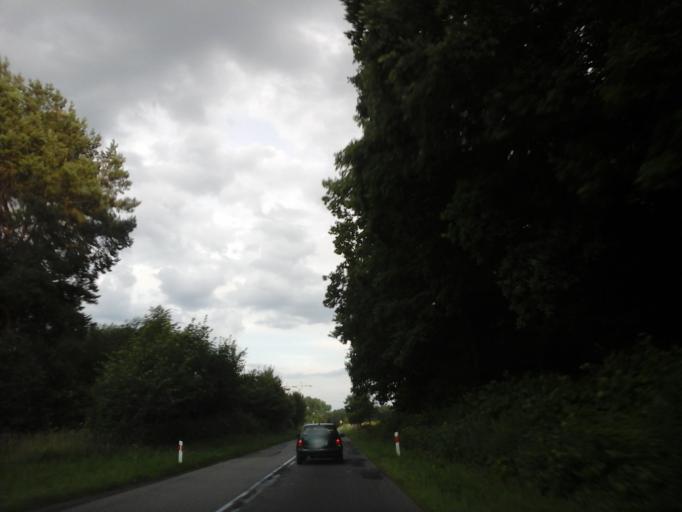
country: PL
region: West Pomeranian Voivodeship
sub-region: Powiat kamienski
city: Golczewo
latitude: 53.8164
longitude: 14.9951
